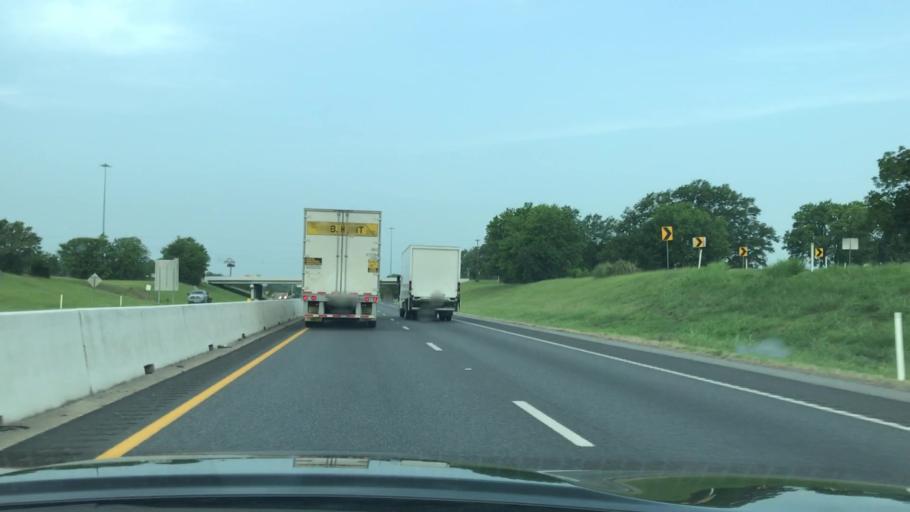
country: US
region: Texas
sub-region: Gregg County
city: Longview
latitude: 32.4469
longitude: -94.7183
